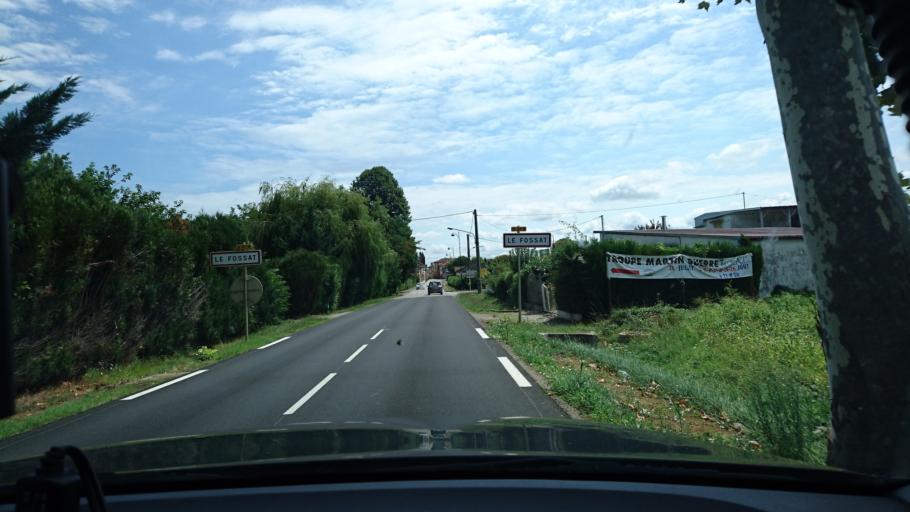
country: FR
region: Midi-Pyrenees
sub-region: Departement de la Haute-Garonne
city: Gaillac-Toulza
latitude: 43.1771
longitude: 1.4057
